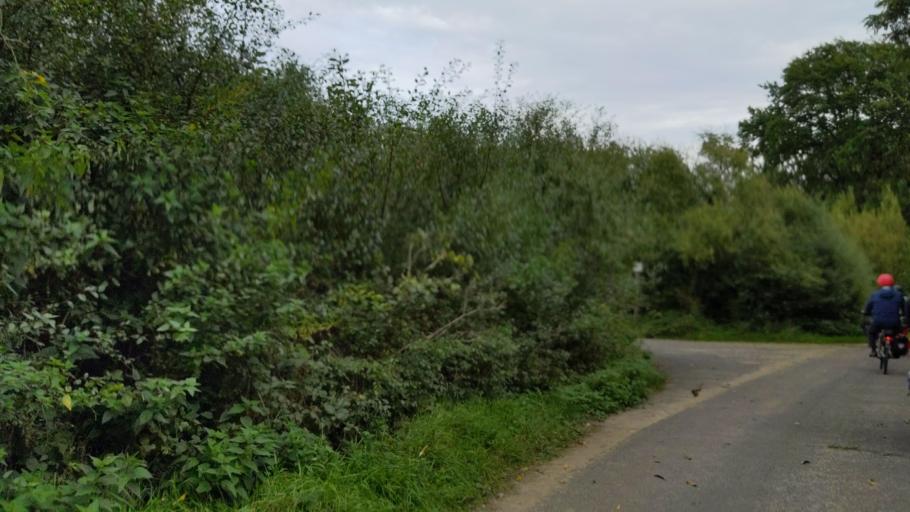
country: DE
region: Schleswig-Holstein
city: Mechow
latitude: 53.7306
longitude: 10.8070
